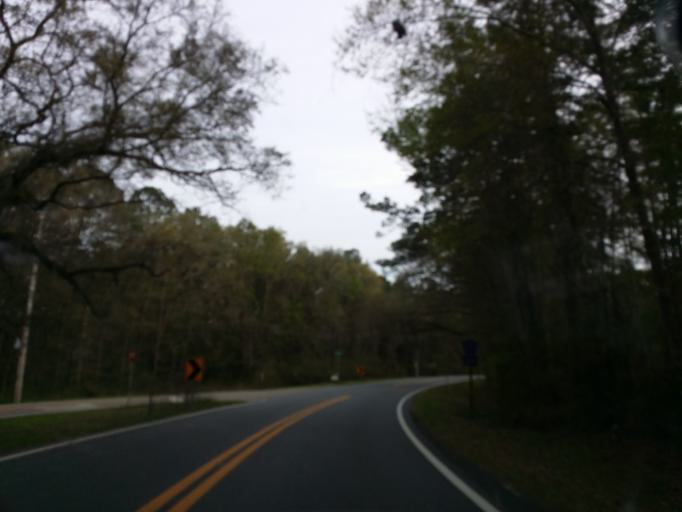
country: US
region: Florida
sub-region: Leon County
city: Tallahassee
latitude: 30.5350
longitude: -84.1303
